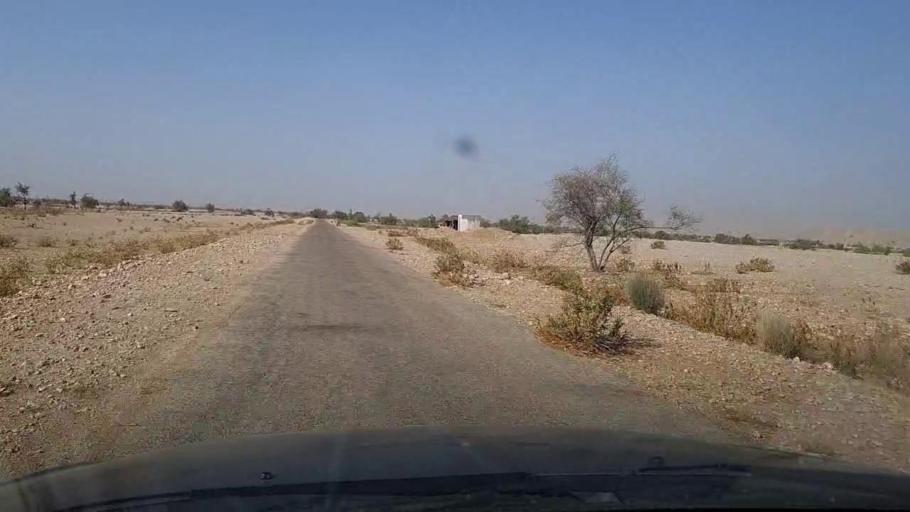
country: PK
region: Sindh
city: Sann
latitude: 25.8902
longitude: 67.9890
